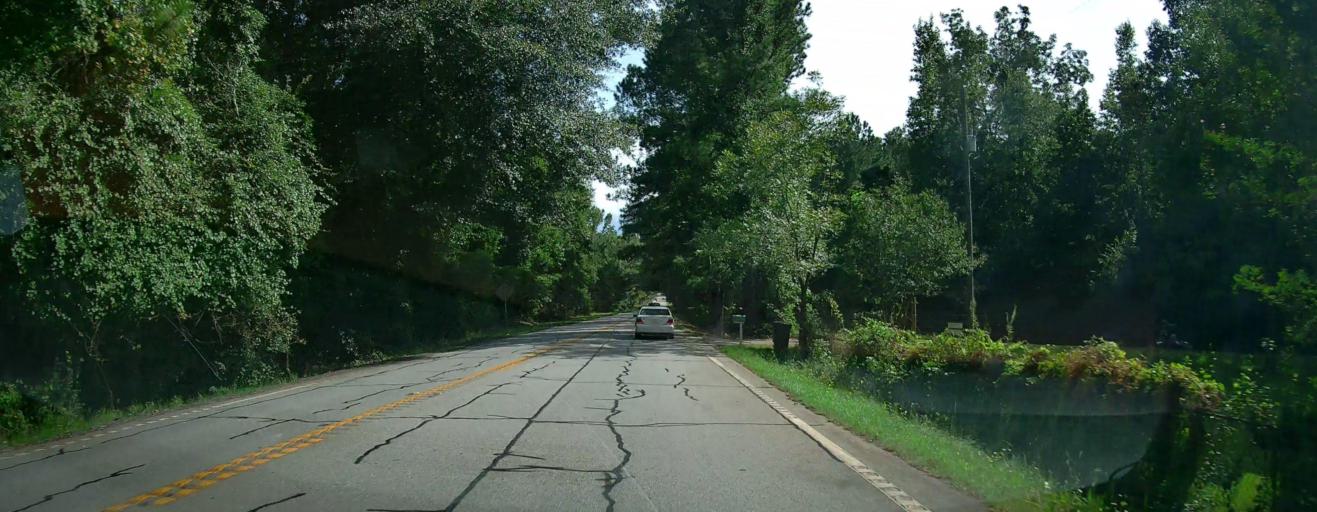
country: US
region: Georgia
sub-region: Harris County
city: Hamilton
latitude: 32.6951
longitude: -84.8566
